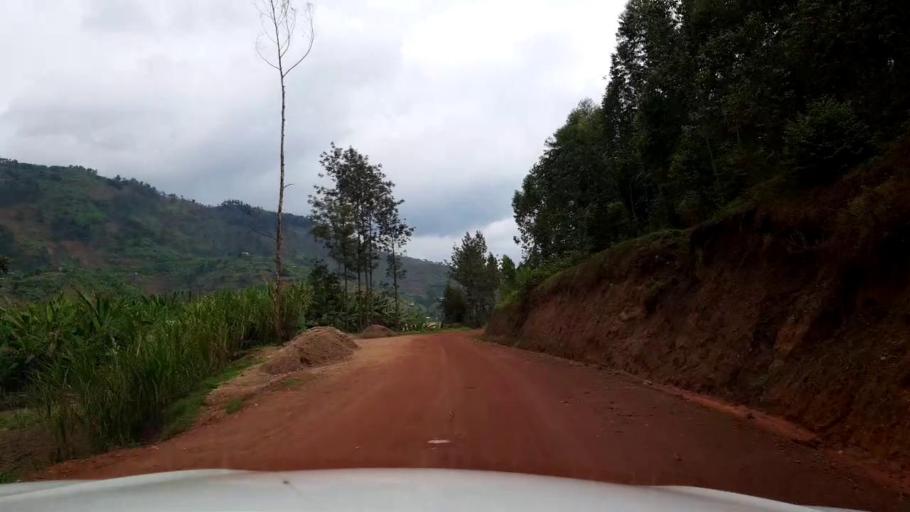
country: RW
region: Northern Province
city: Musanze
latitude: -1.6694
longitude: 29.8009
